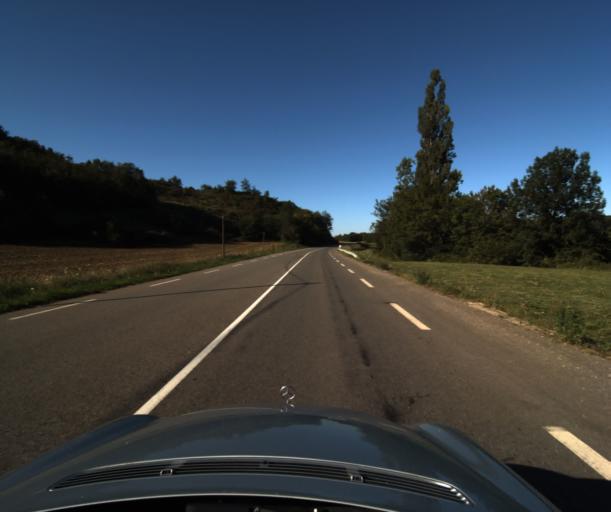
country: FR
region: Midi-Pyrenees
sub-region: Departement de l'Ariege
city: Mirepoix
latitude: 43.0112
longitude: 1.8872
